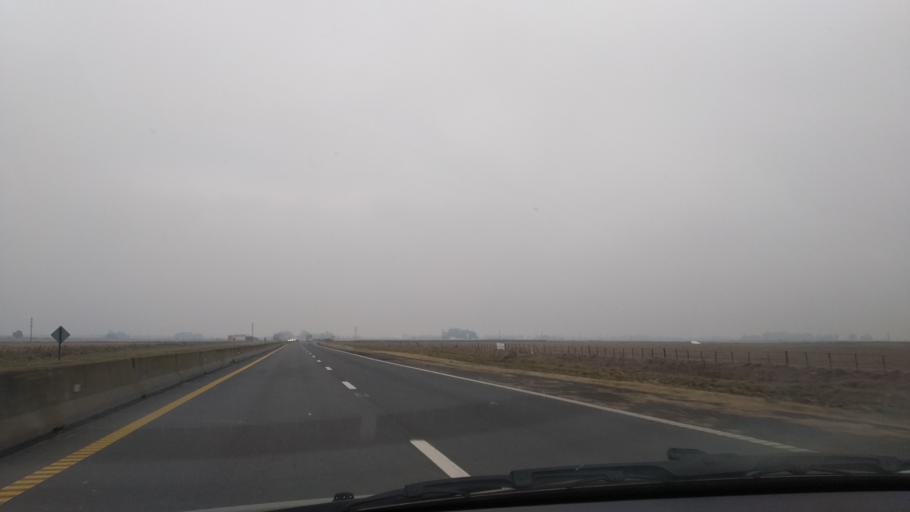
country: AR
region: Buenos Aires
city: Olavarria
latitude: -36.8544
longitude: -60.1135
